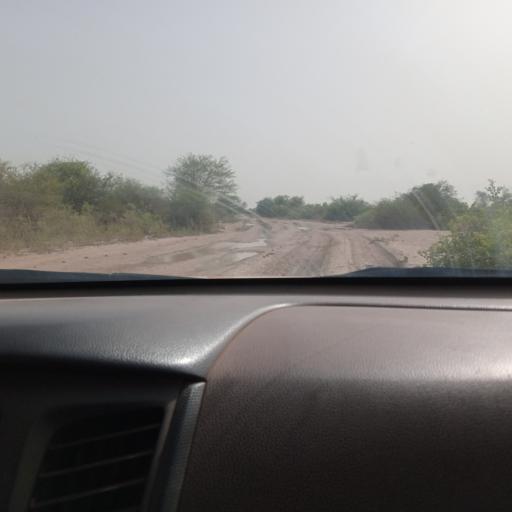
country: ML
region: Mopti
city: Tenenkou
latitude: 14.2079
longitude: -5.0122
